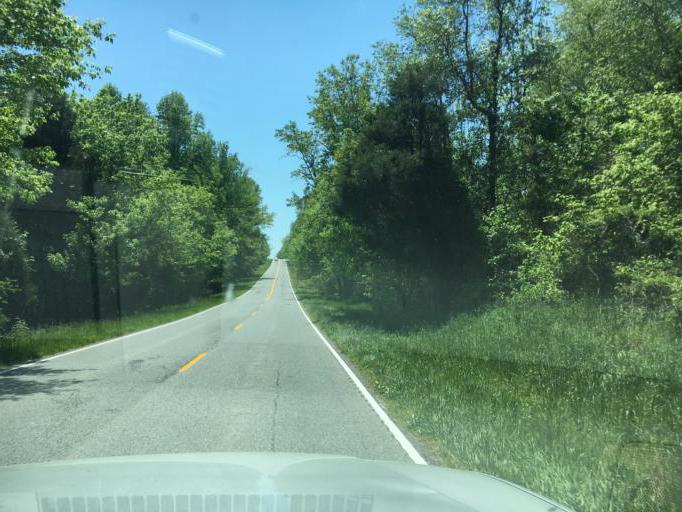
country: US
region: South Carolina
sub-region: Cherokee County
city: Blacksburg
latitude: 35.1441
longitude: -81.5764
